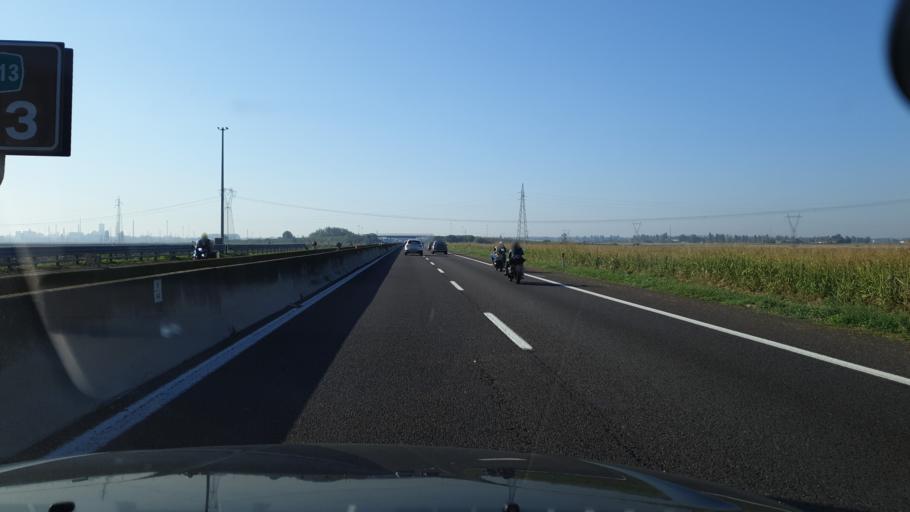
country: IT
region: Veneto
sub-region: Provincia di Rovigo
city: Occhiobello
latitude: 44.8902
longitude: 11.5701
